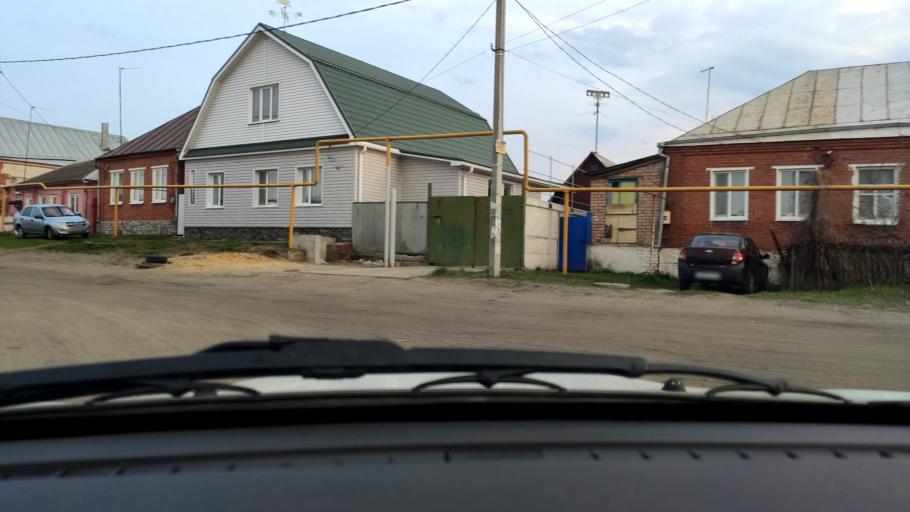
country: RU
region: Voronezj
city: Somovo
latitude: 51.7506
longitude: 39.3340
